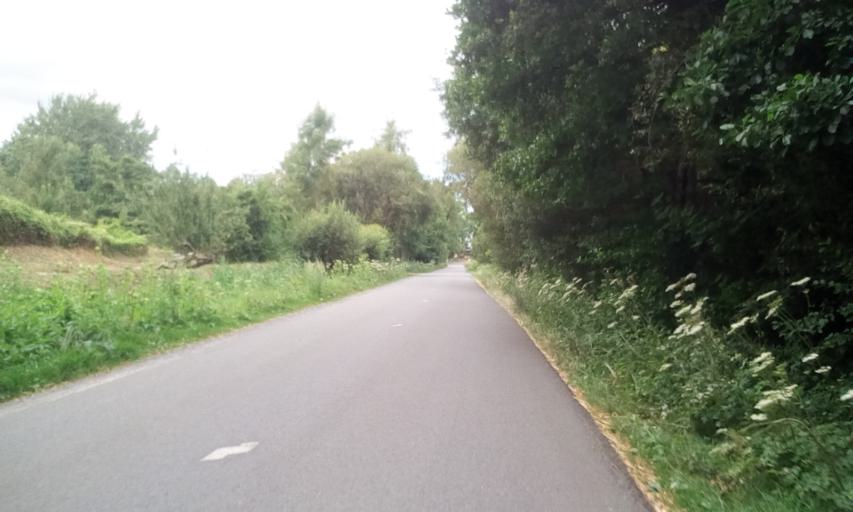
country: FR
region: Lower Normandy
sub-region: Departement du Calvados
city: Bellengreville
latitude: 49.1150
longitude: -0.2234
